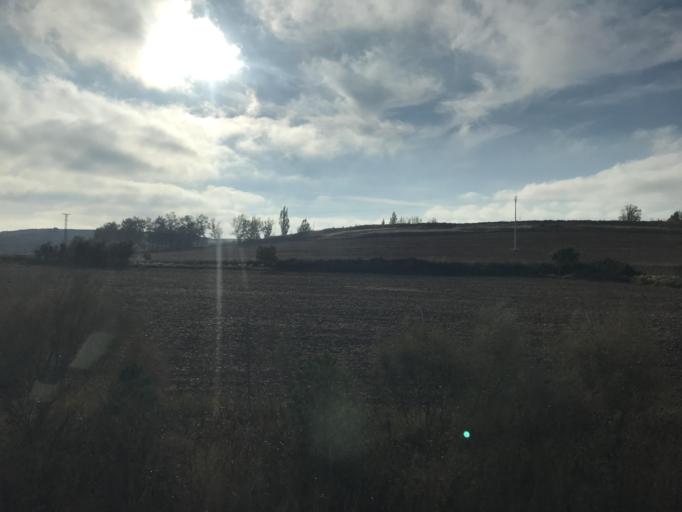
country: ES
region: Castille and Leon
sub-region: Provincia de Burgos
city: San Mames de Burgos
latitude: 42.3354
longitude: -3.8009
